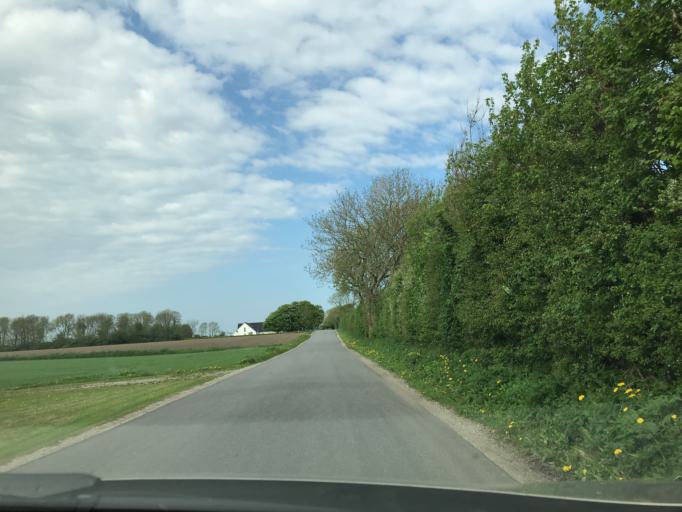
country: DK
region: South Denmark
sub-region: Middelfart Kommune
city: Norre Aby
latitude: 55.3821
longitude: 9.8496
